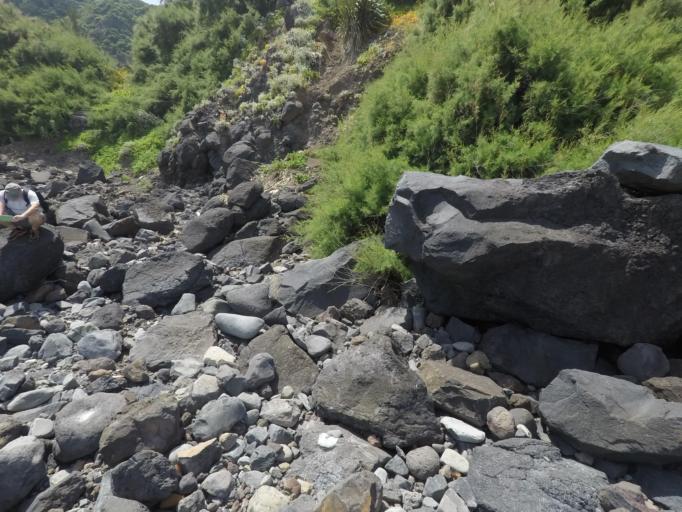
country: PT
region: Madeira
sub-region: Sao Vicente
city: Sao Vicente
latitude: 32.8298
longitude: -16.9868
